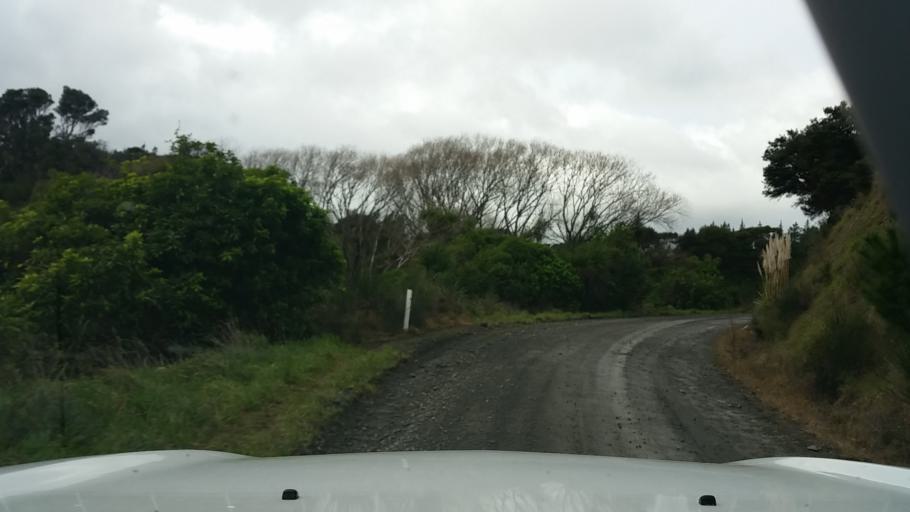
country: NZ
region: Wellington
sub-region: South Wairarapa District
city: Waipawa
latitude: -41.3929
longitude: 175.2263
